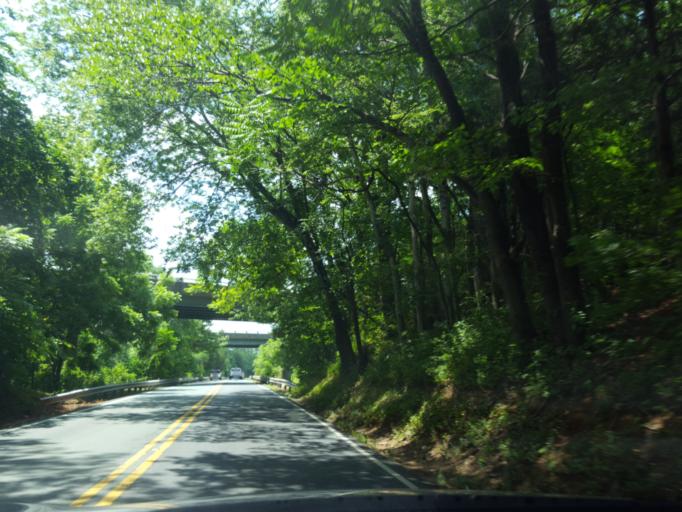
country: US
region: Virginia
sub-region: City of Charlottesville
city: Charlottesville
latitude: 38.0154
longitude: -78.3899
